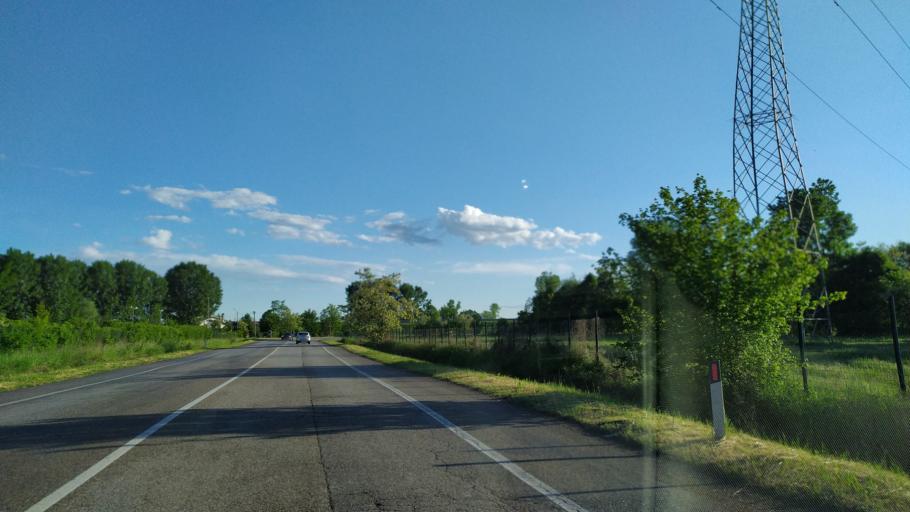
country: IT
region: Veneto
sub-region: Provincia di Padova
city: Taggi
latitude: 45.4528
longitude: 11.8344
